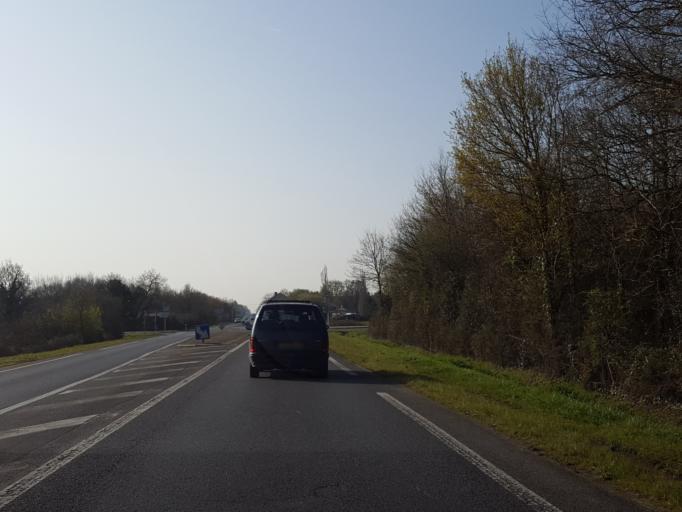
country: FR
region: Pays de la Loire
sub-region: Departement de la Loire-Atlantique
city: Le Bignon
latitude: 47.0925
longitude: -1.5304
